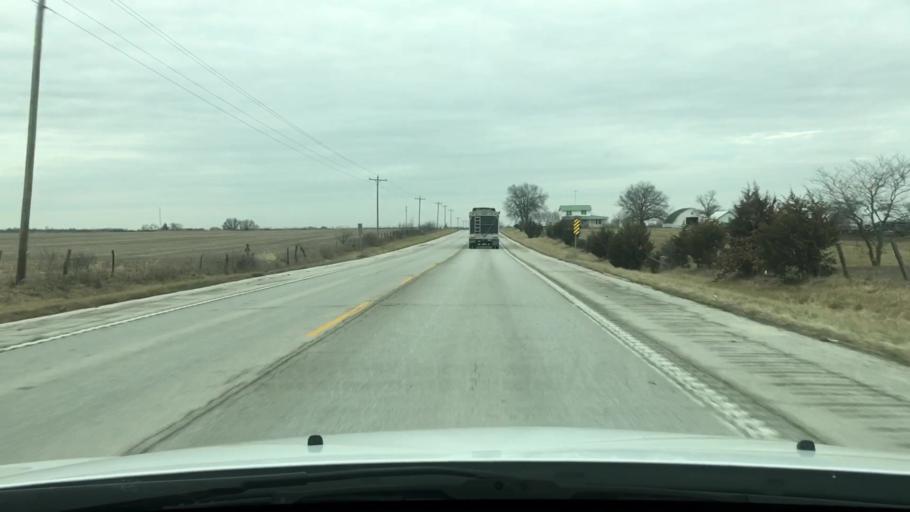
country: US
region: Missouri
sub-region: Montgomery County
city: Wellsville
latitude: 39.1744
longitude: -91.6476
